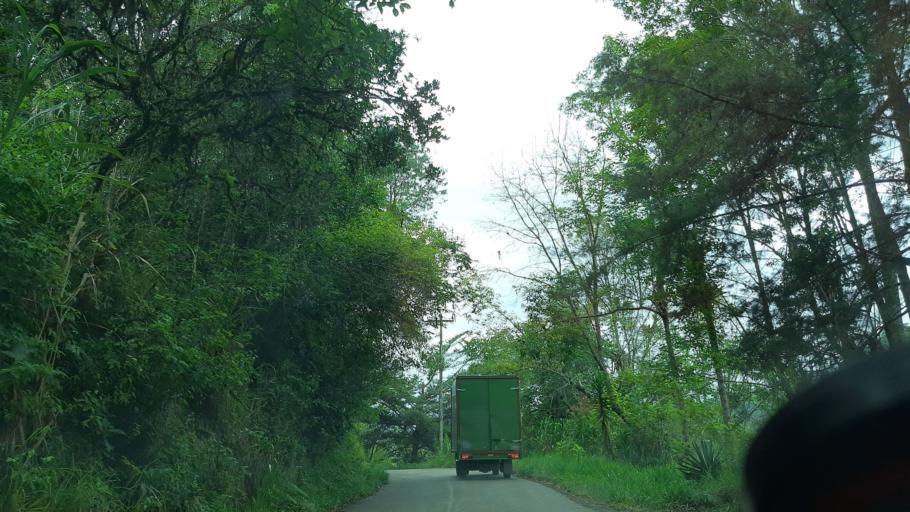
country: CO
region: Cundinamarca
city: Tenza
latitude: 5.0751
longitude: -73.4128
